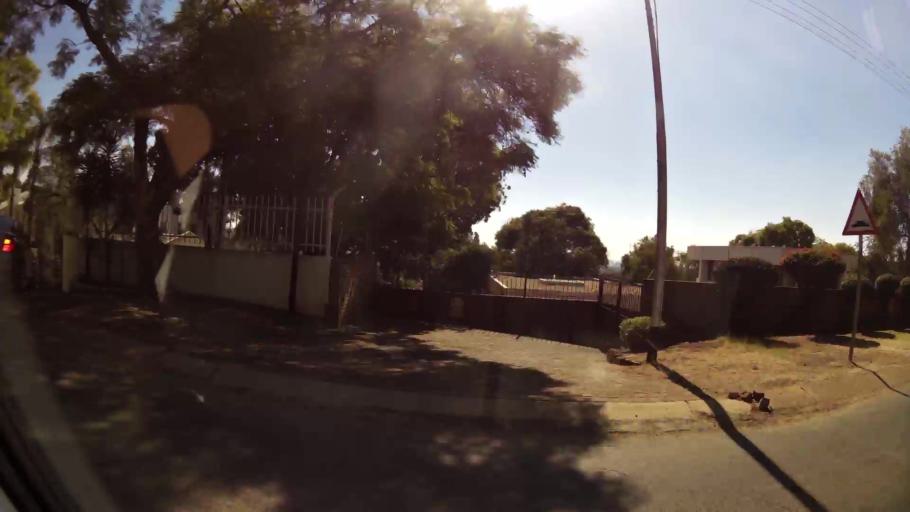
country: ZA
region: Gauteng
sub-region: City of Tshwane Metropolitan Municipality
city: Pretoria
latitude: -25.7834
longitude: 28.2442
